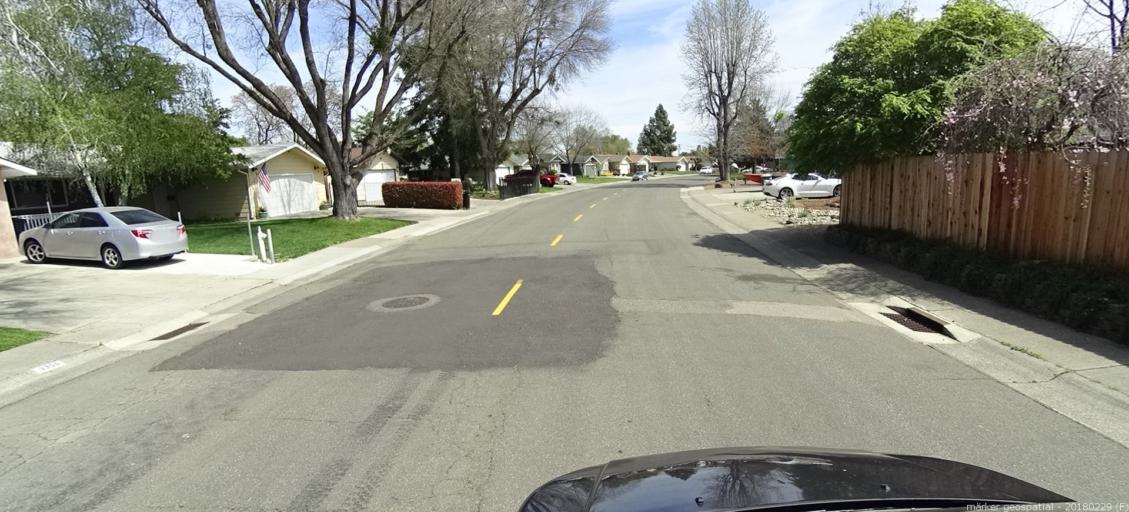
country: US
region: California
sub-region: Sacramento County
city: Rosemont
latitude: 38.5517
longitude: -121.3597
